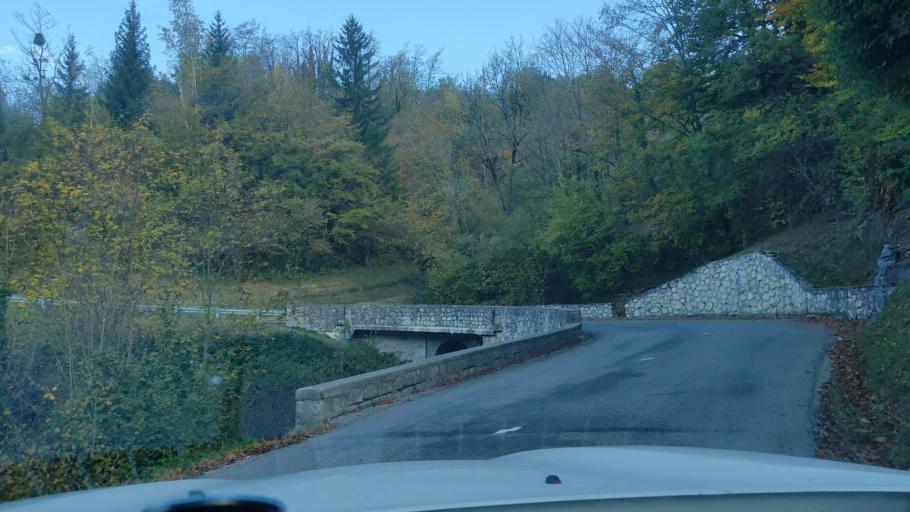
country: FR
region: Rhone-Alpes
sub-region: Departement de la Savoie
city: Barby
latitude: 45.5804
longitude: 6.0401
